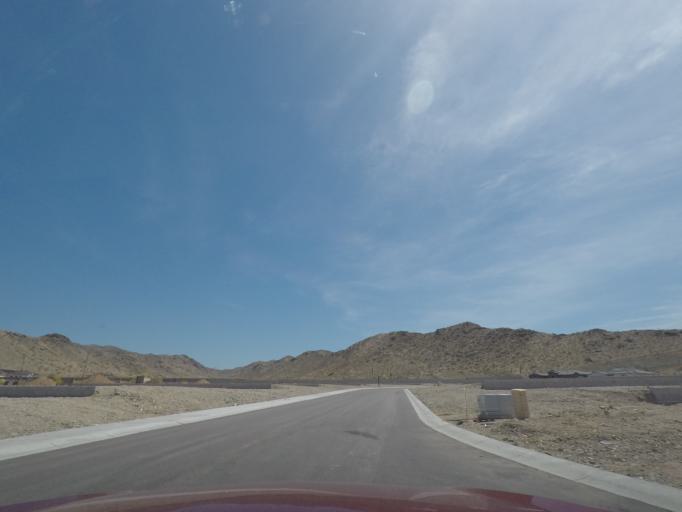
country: US
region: Arizona
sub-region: Maricopa County
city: Laveen
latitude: 33.2989
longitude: -112.1381
